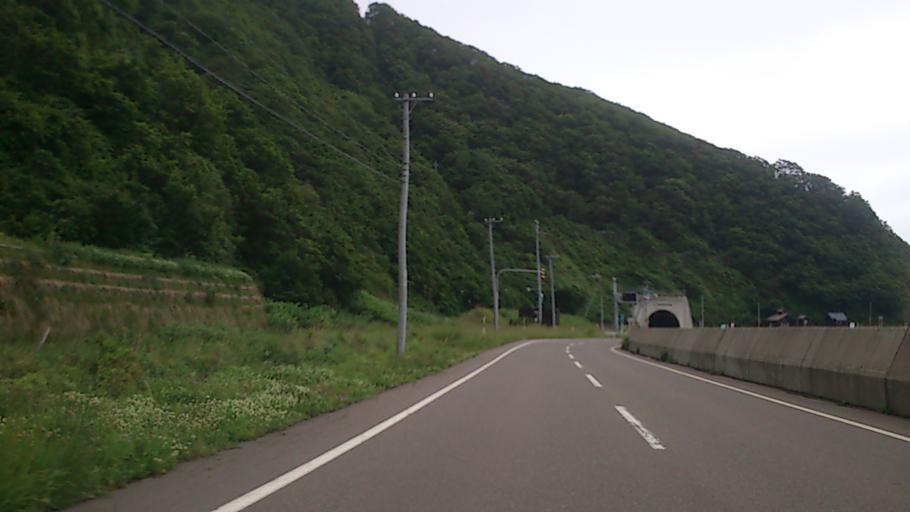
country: JP
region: Hokkaido
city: Kamiiso
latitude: 42.2703
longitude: 139.7849
